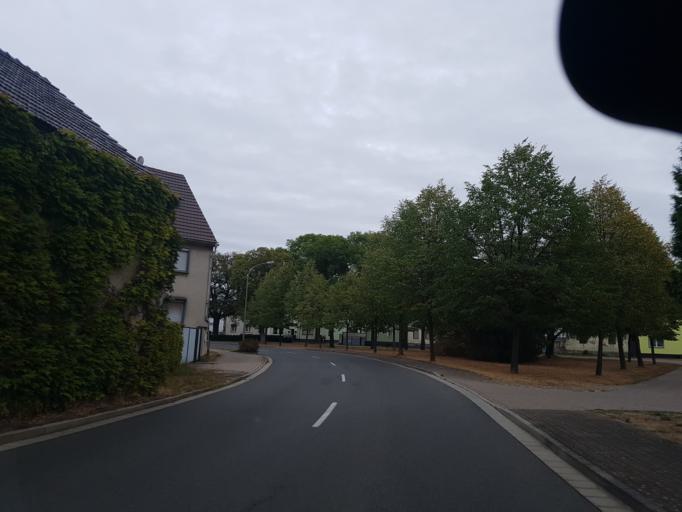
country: DE
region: Saxony-Anhalt
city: Prettin
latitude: 51.7002
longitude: 12.8903
